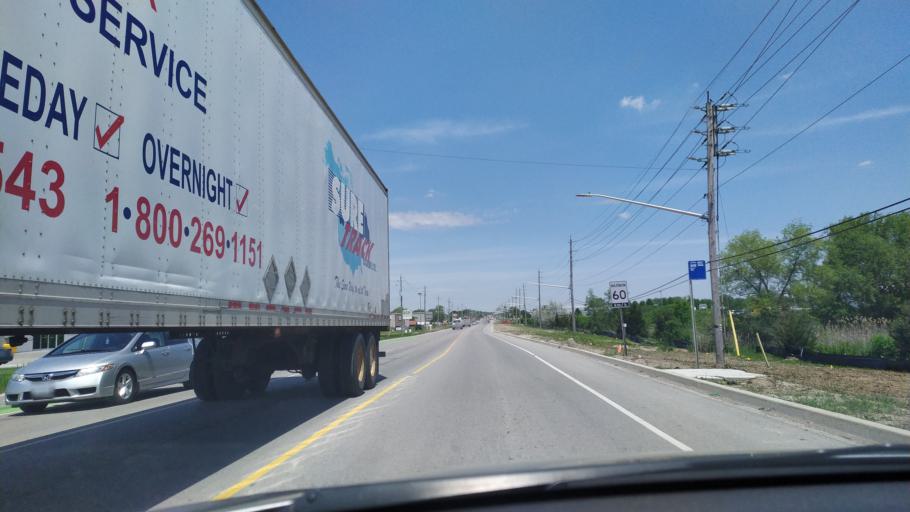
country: CA
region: Ontario
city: London
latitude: 42.9235
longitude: -81.2479
